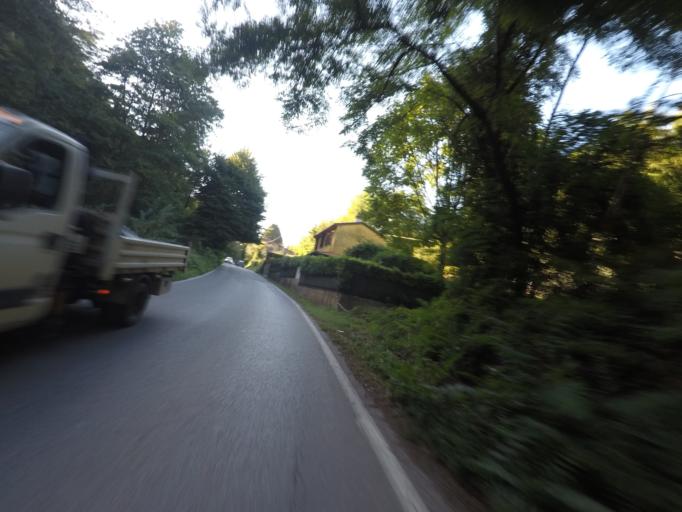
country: IT
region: Tuscany
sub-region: Provincia di Lucca
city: Stiava
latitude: 43.9061
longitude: 10.3506
